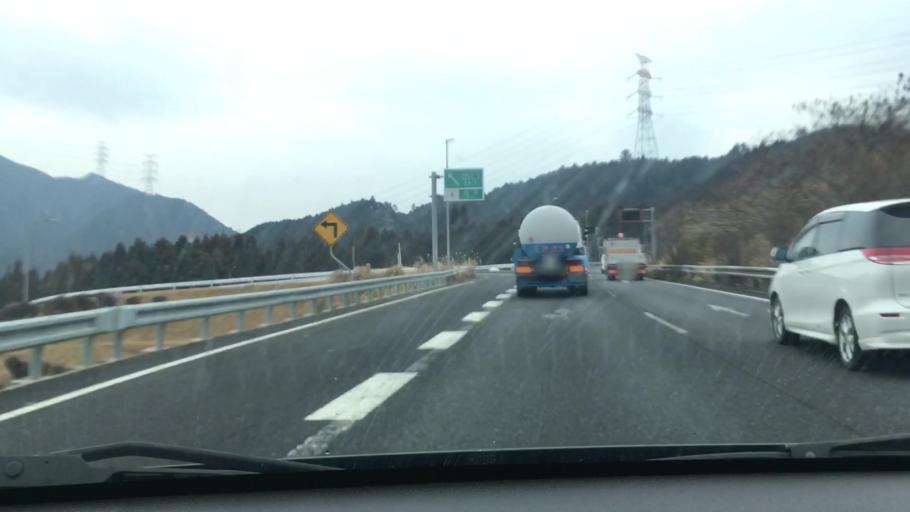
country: JP
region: Mie
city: Kameyama
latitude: 34.8373
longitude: 136.3399
